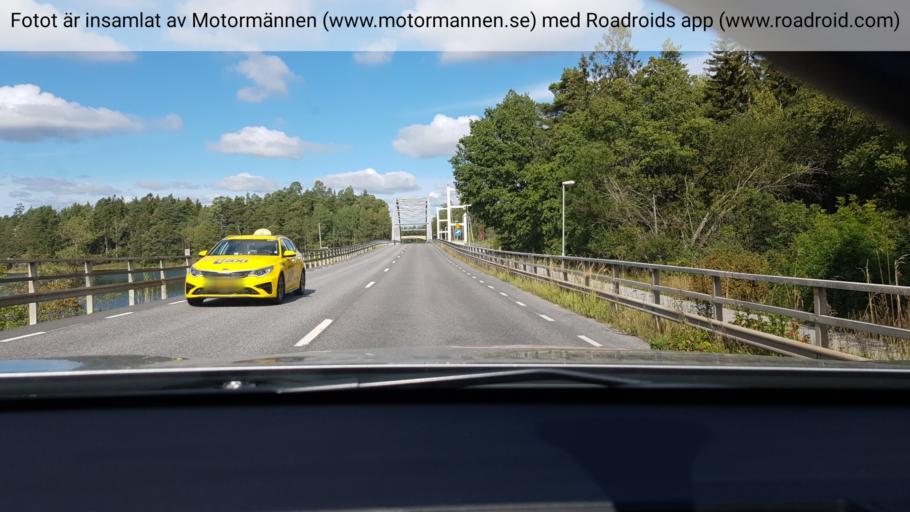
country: SE
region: Stockholm
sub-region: Vaxholms Kommun
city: Resaro
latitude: 59.4079
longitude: 18.3169
